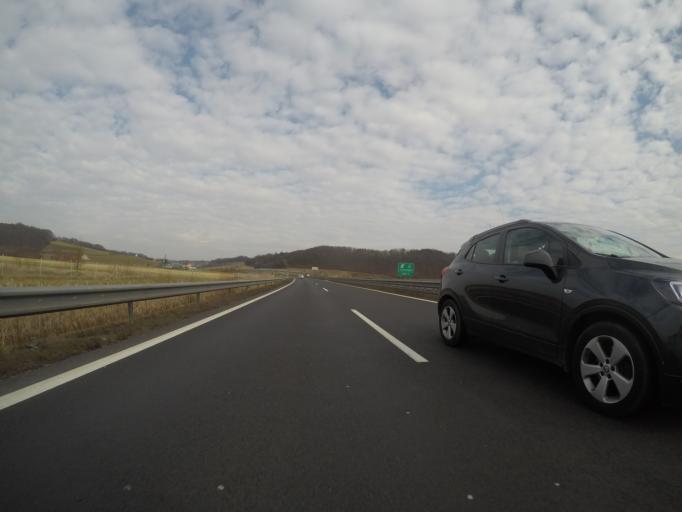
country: SI
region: Cerkvenjak
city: Cerkvenjak
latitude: 46.5551
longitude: 15.9093
